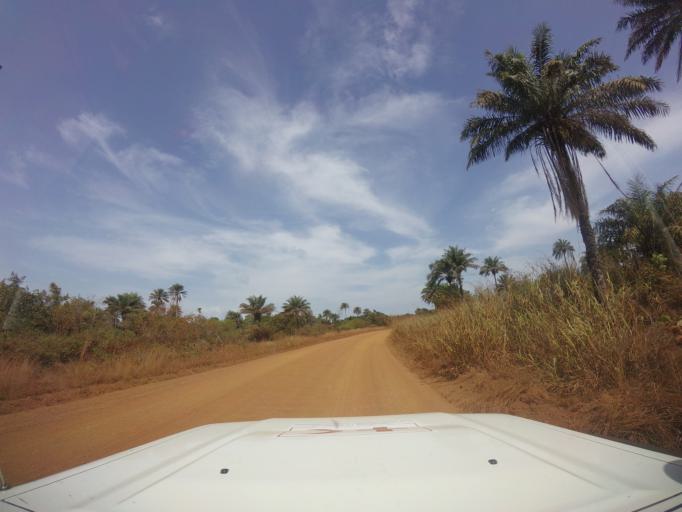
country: LR
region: Grand Cape Mount
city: Robertsport
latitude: 6.7069
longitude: -11.2965
